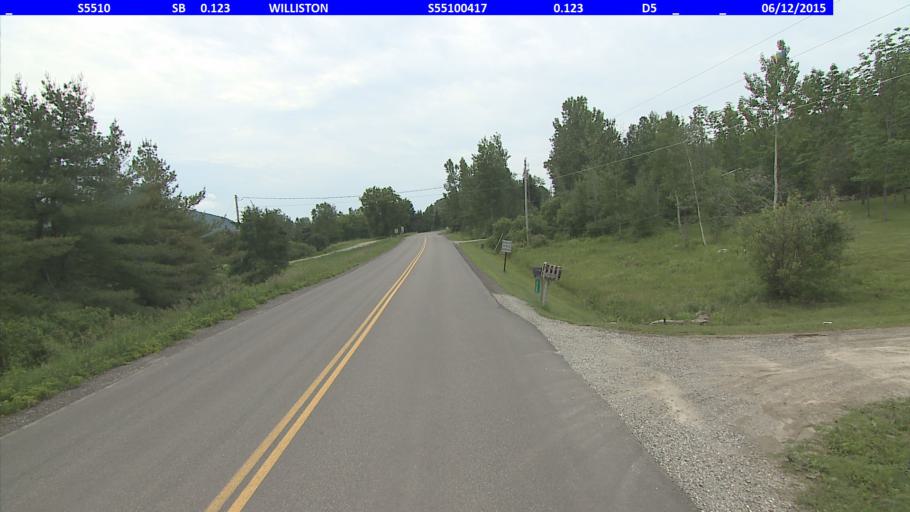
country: US
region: Vermont
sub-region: Chittenden County
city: Hinesburg
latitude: 44.3746
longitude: -73.0937
